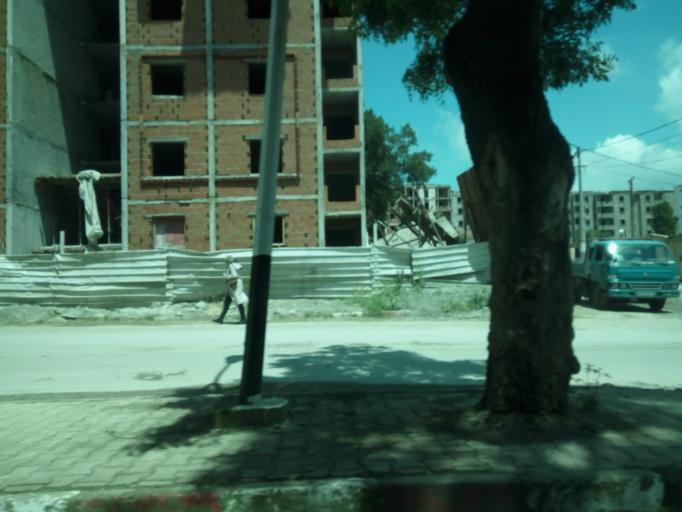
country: DZ
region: Tipaza
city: Saoula
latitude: 36.7314
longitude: 2.9952
